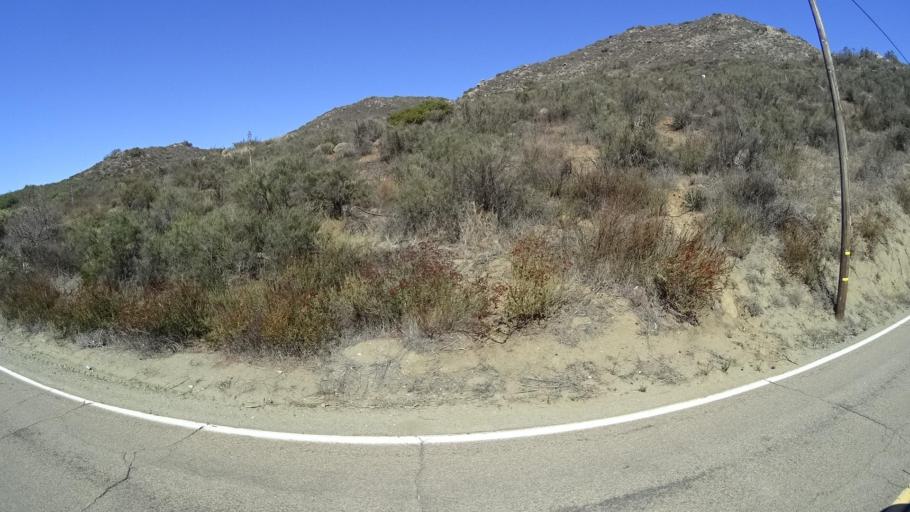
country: US
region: California
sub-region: San Diego County
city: Alpine
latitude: 32.7989
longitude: -116.7520
